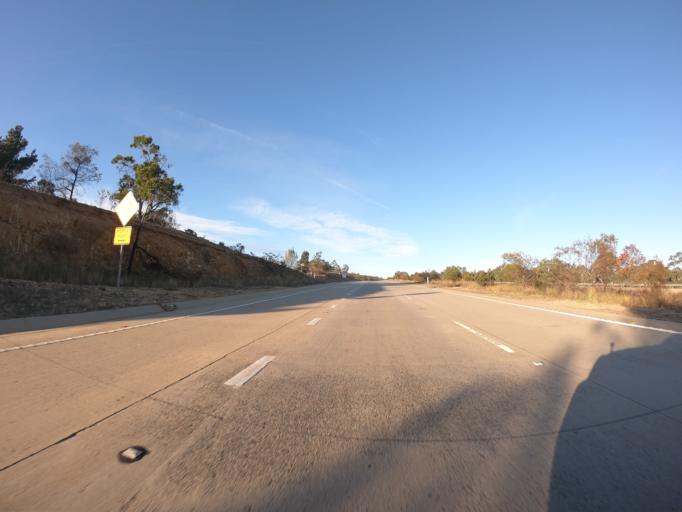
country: AU
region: New South Wales
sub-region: Yass Valley
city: Gundaroo
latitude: -35.1024
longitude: 149.3740
